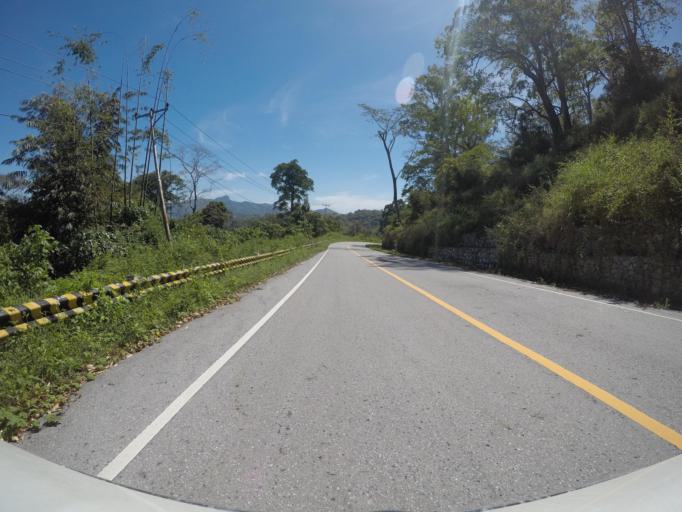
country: TL
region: Manufahi
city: Same
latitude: -8.8847
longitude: 125.9872
